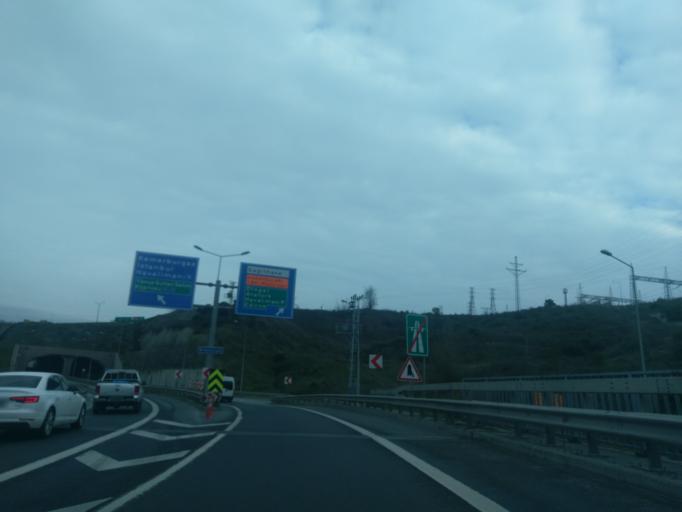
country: TR
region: Istanbul
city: Sisli
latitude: 41.0949
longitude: 28.9536
